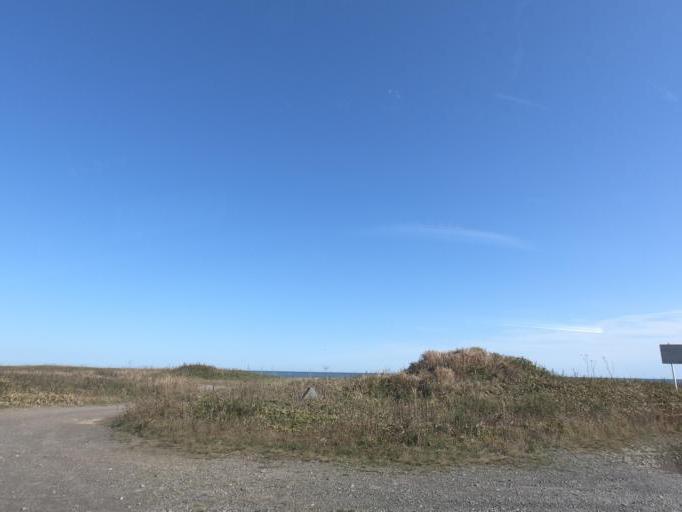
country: JP
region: Hokkaido
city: Obihiro
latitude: 42.6006
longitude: 143.5506
